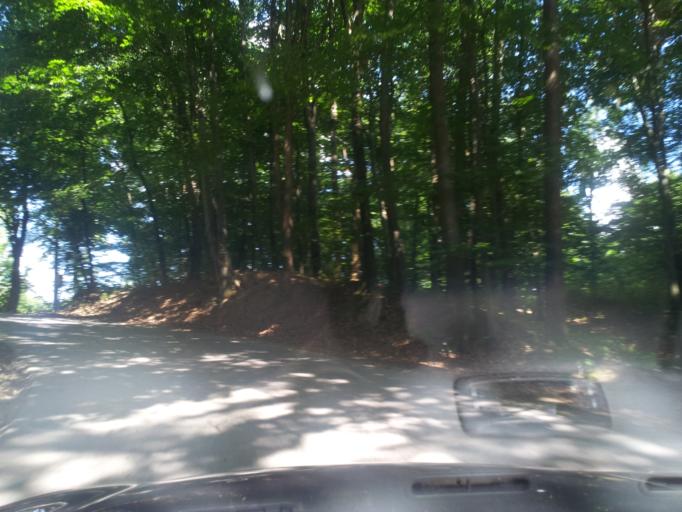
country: HR
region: Karlovacka
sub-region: Grad Karlovac
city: Karlovac
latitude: 45.4662
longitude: 15.4771
